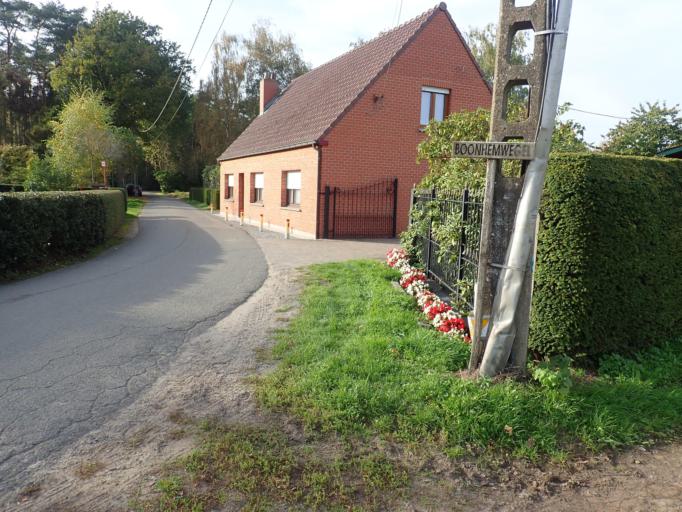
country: BE
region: Flanders
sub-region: Provincie Oost-Vlaanderen
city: Sint-Niklaas
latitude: 51.1689
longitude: 4.0919
